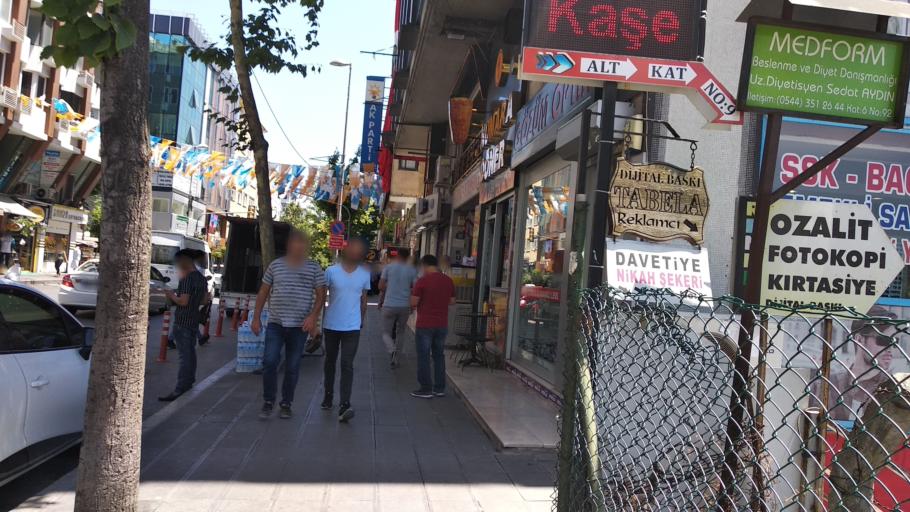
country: TR
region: Istanbul
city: Yakuplu
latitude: 40.9798
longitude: 28.7222
